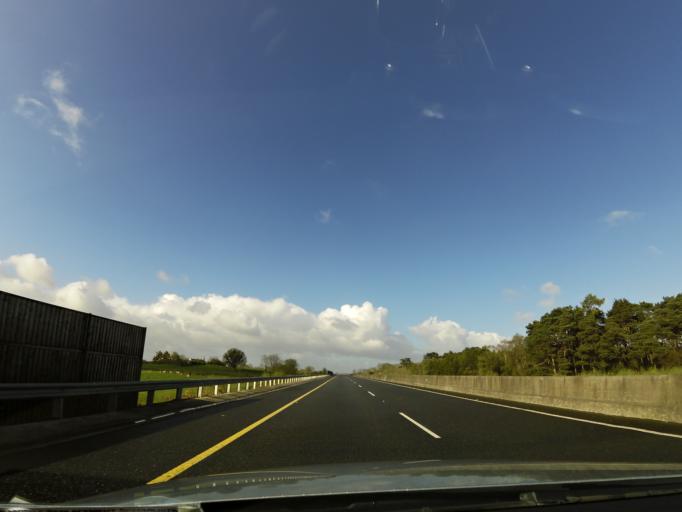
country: IE
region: Munster
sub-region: North Tipperary
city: Newport
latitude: 52.7384
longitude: -8.4458
